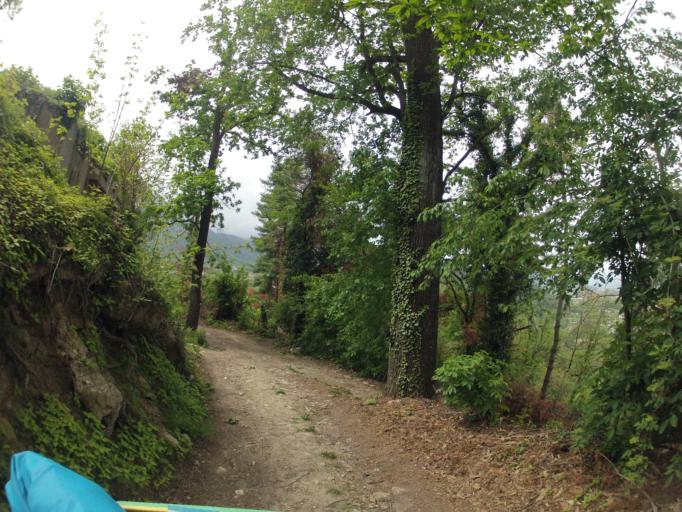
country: IT
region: Piedmont
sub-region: Provincia di Cuneo
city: Peveragno
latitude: 44.3343
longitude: 7.6166
